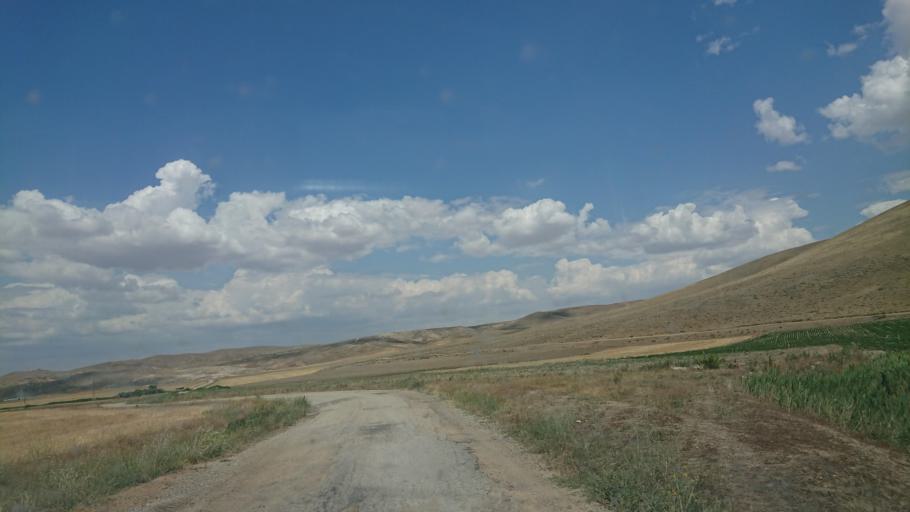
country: TR
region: Aksaray
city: Sariyahsi
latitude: 38.9880
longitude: 33.9084
